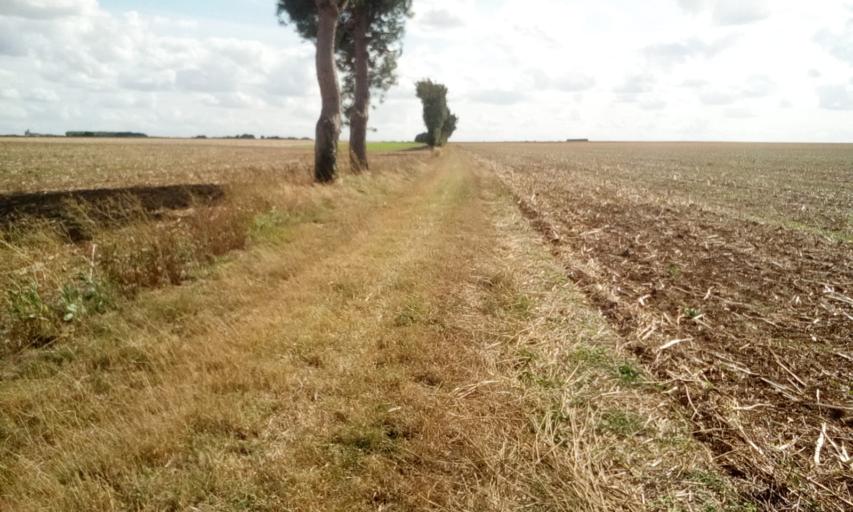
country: FR
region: Lower Normandy
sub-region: Departement du Calvados
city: Saint-Sylvain
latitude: 49.0866
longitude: -0.1968
